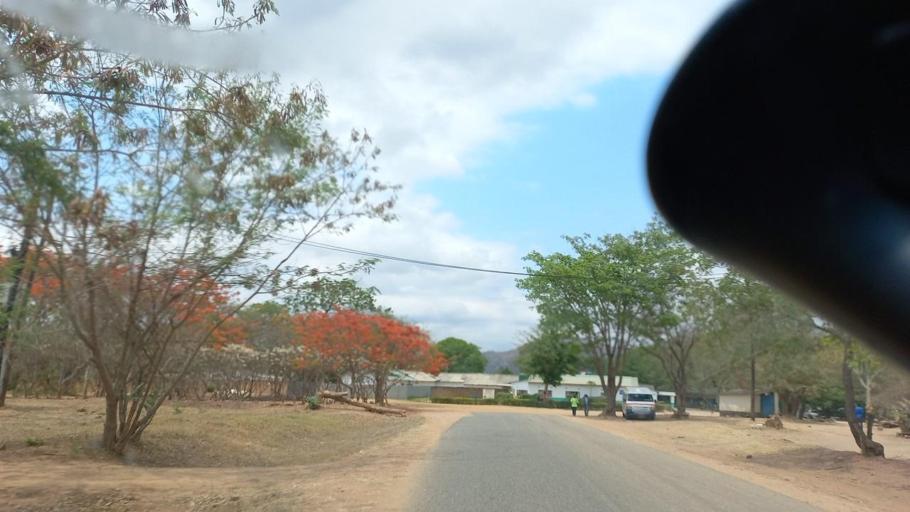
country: ZM
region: Lusaka
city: Luangwa
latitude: -15.1074
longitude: 29.7252
